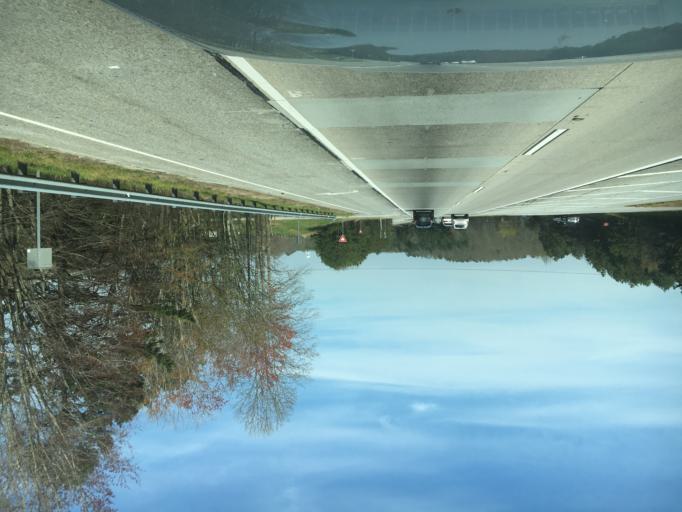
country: US
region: Georgia
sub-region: Hall County
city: Lula
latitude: 34.3828
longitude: -83.7099
